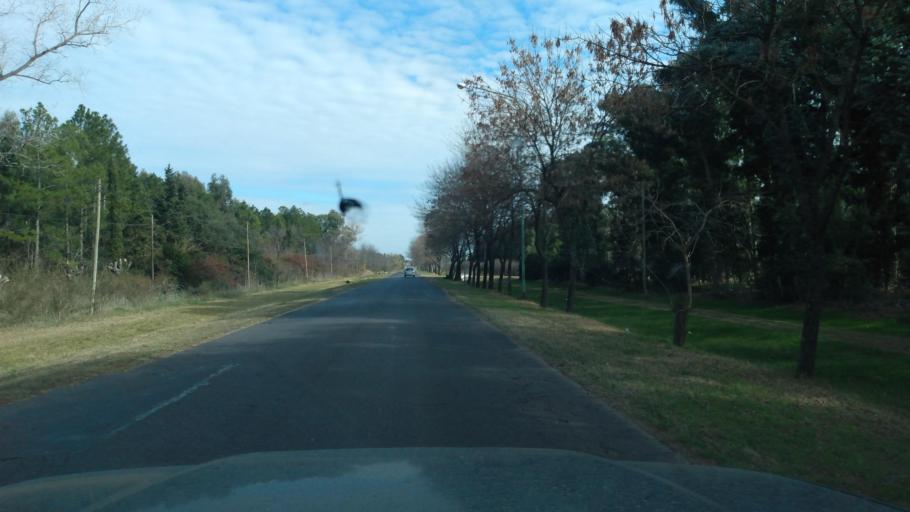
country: AR
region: Buenos Aires
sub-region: Partido de Lujan
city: Lujan
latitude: -34.5733
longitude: -59.1590
